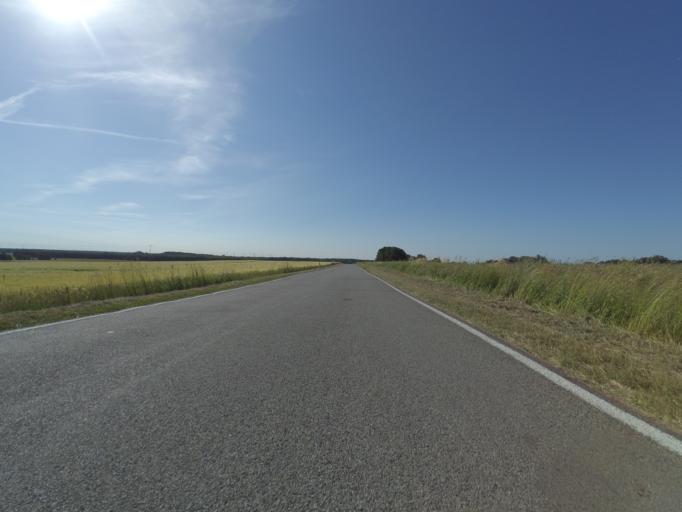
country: DE
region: Brandenburg
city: Putlitz
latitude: 53.3038
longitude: 12.0451
